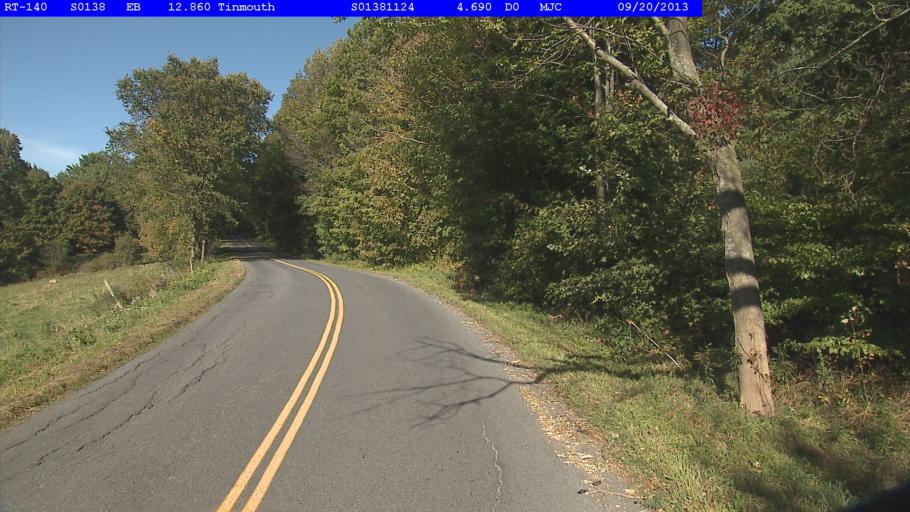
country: US
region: Vermont
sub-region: Rutland County
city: West Rutland
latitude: 43.4510
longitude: -73.0258
